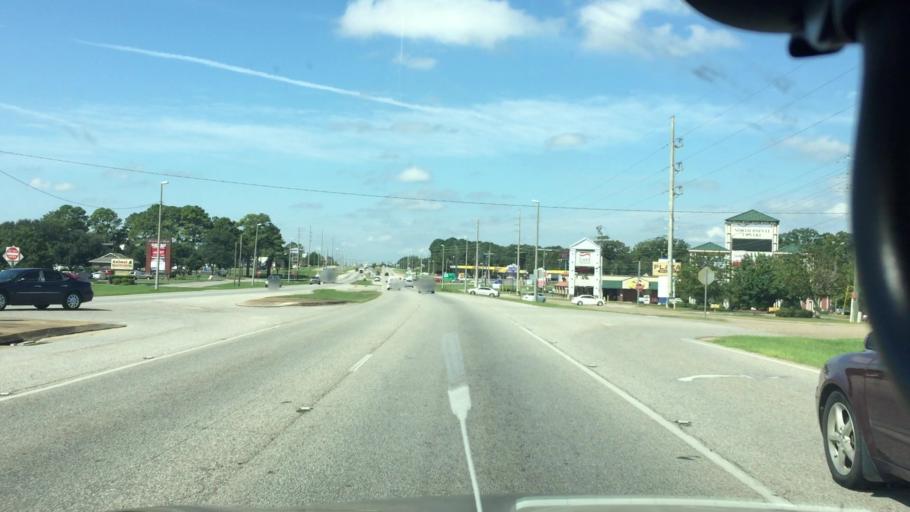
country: US
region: Alabama
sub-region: Coffee County
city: Enterprise
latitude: 31.3350
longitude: -85.8548
